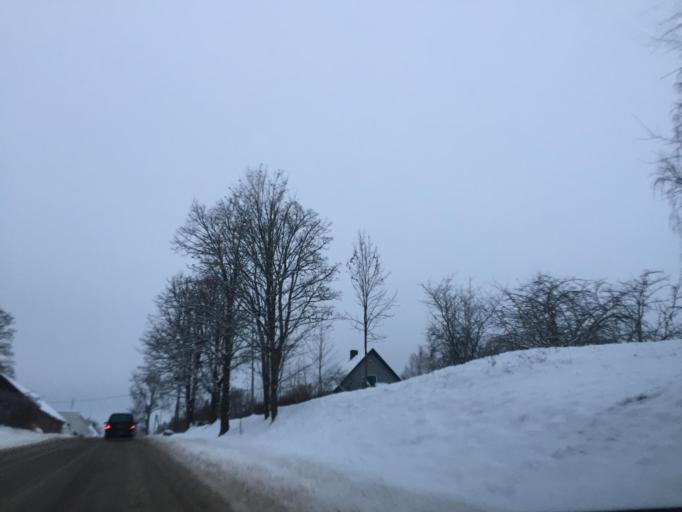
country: LV
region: Smiltene
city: Smiltene
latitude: 57.4370
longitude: 25.7834
